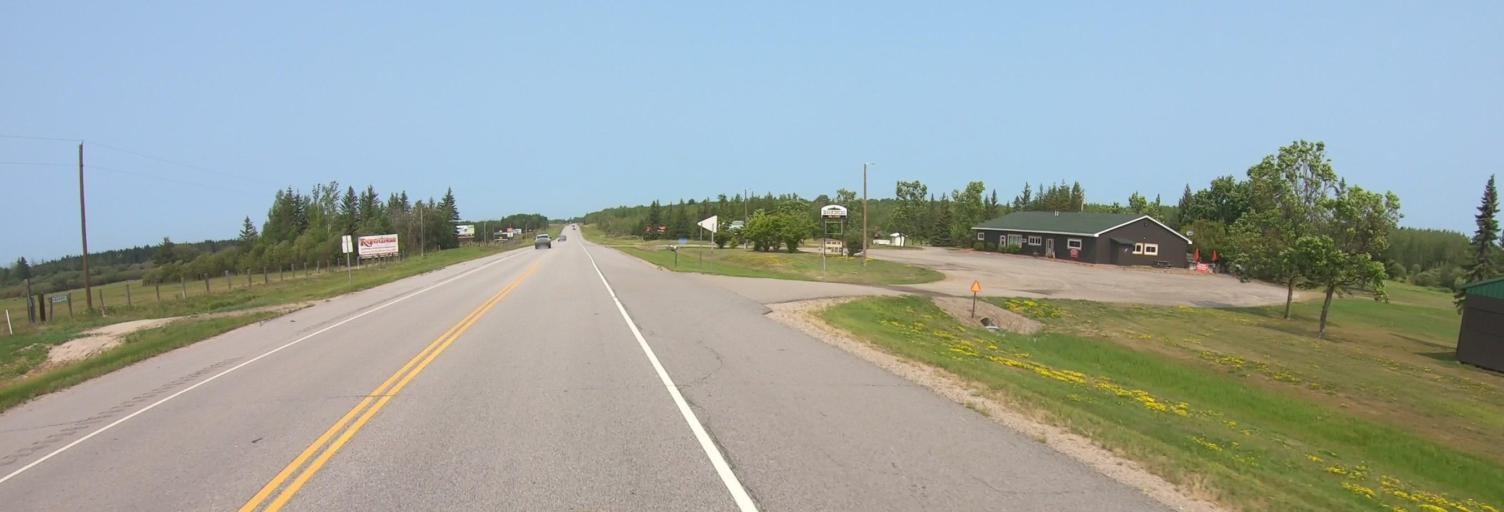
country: CA
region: Ontario
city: Fort Frances
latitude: 48.4129
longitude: -93.2063
